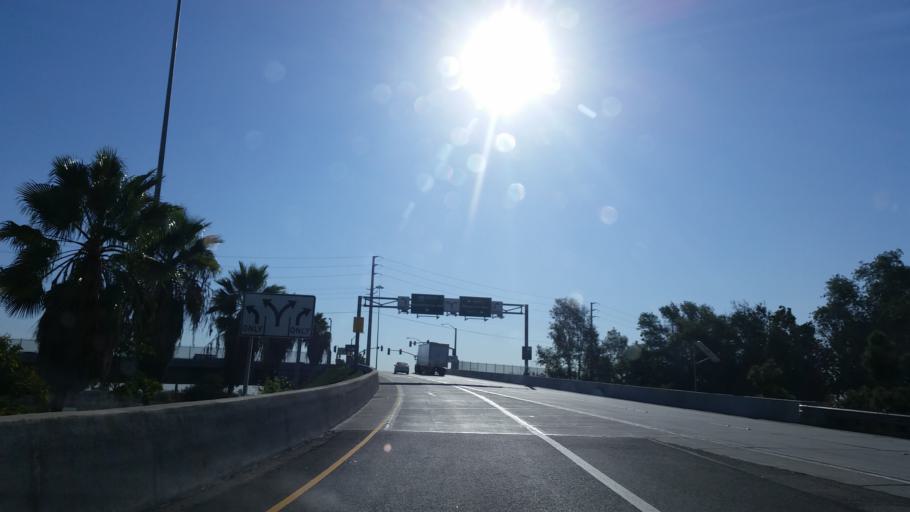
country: US
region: California
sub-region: Orange County
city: Buena Park
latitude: 33.8552
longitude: -117.9778
